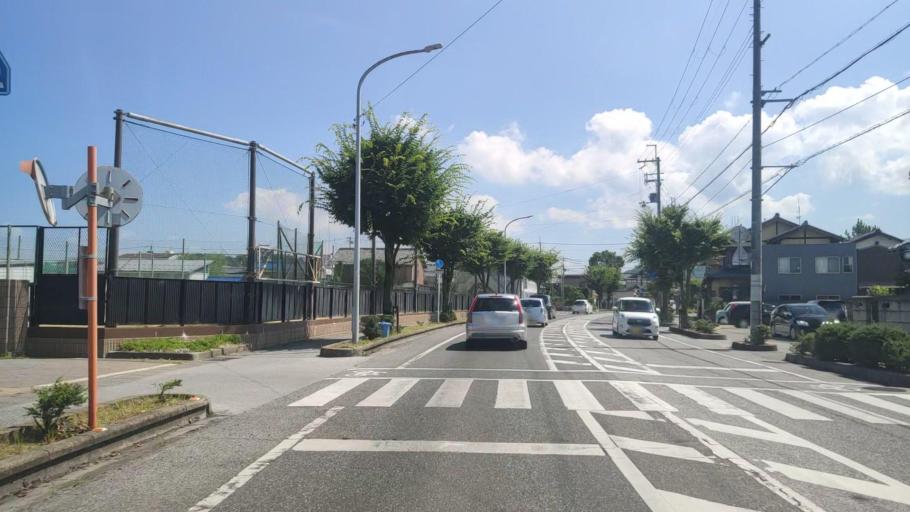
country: JP
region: Shiga Prefecture
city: Hikone
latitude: 35.2697
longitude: 136.2476
